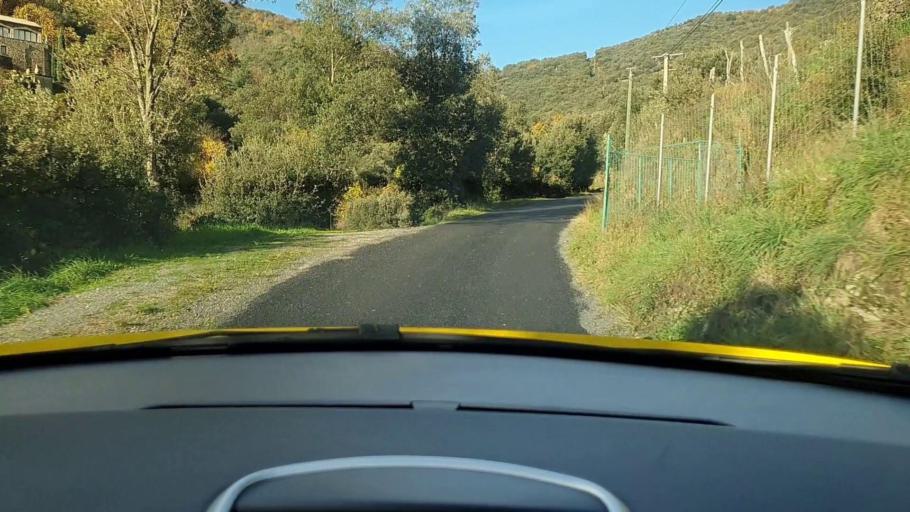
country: FR
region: Languedoc-Roussillon
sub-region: Departement du Gard
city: Sumene
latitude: 44.0361
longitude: 3.7327
